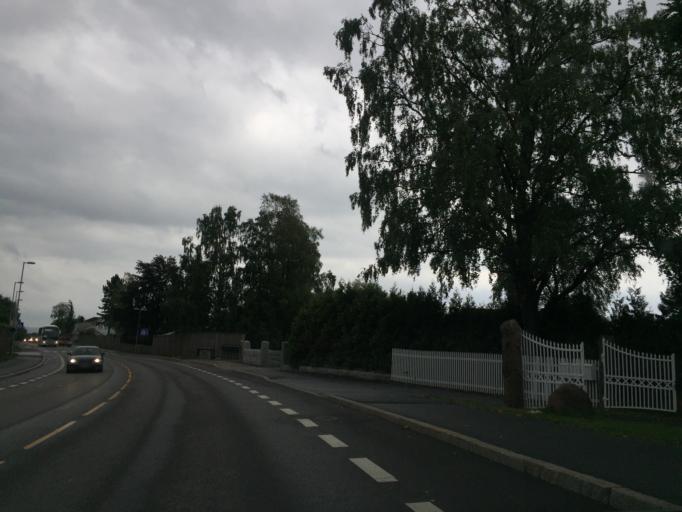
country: NO
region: Oslo
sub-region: Oslo
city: Sjolyststranda
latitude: 59.9473
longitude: 10.6765
